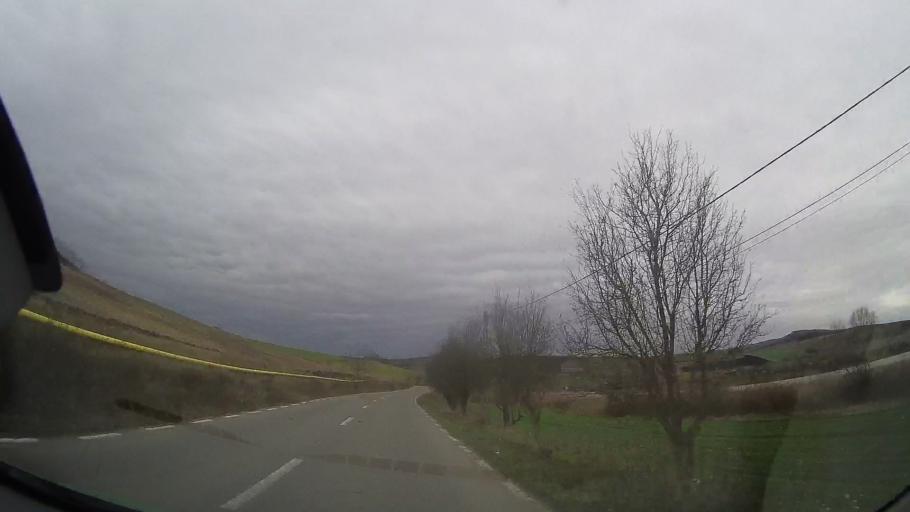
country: RO
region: Cluj
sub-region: Comuna Geaca
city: Geaca
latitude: 46.8410
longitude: 24.1360
